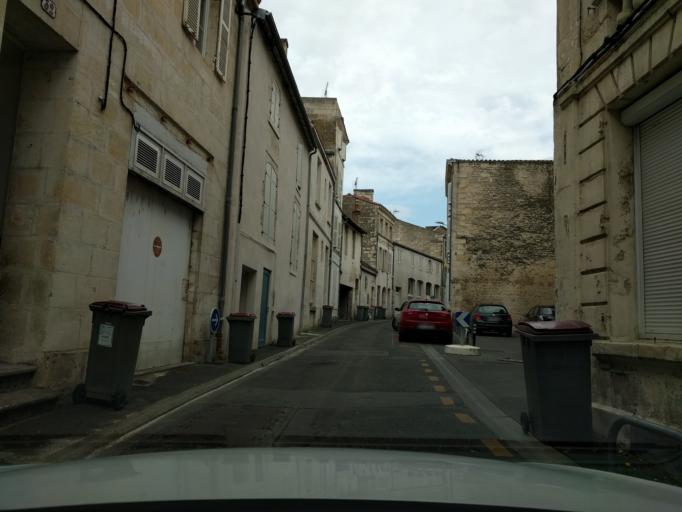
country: FR
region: Poitou-Charentes
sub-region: Departement des Deux-Sevres
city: Niort
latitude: 46.3242
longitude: -0.4607
